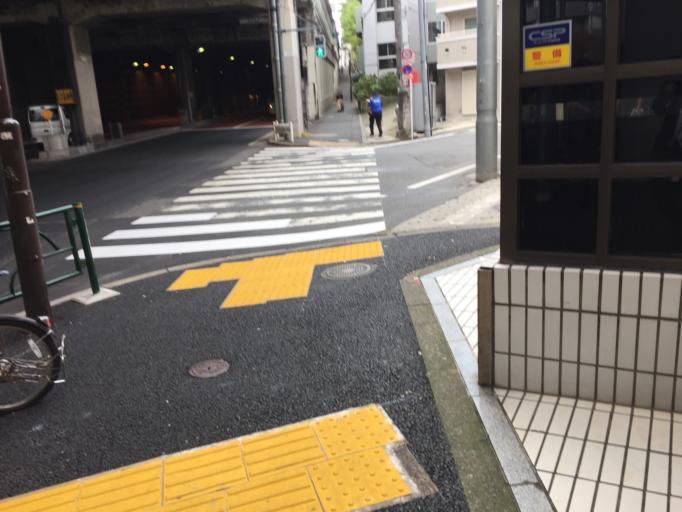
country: JP
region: Tokyo
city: Tokyo
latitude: 35.6418
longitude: 139.7192
